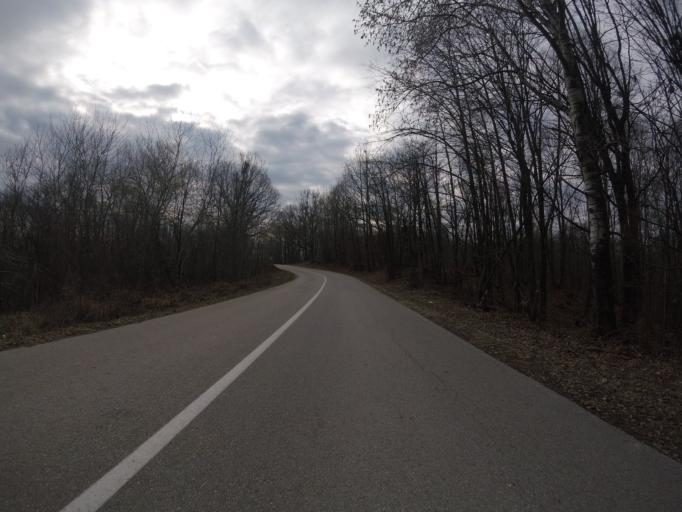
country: HR
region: Zagrebacka
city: Mraclin
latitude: 45.5335
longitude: 16.0572
